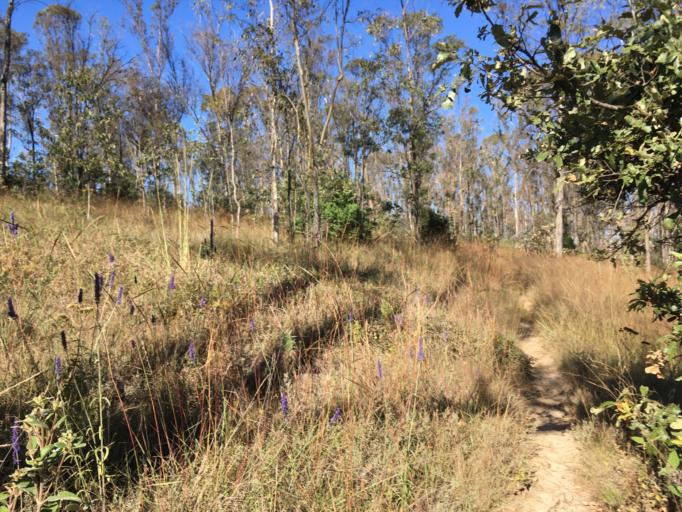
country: MX
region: Michoacan
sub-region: Morelia
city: Montana Monarca (Punta Altozano)
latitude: 19.6680
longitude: -101.1472
